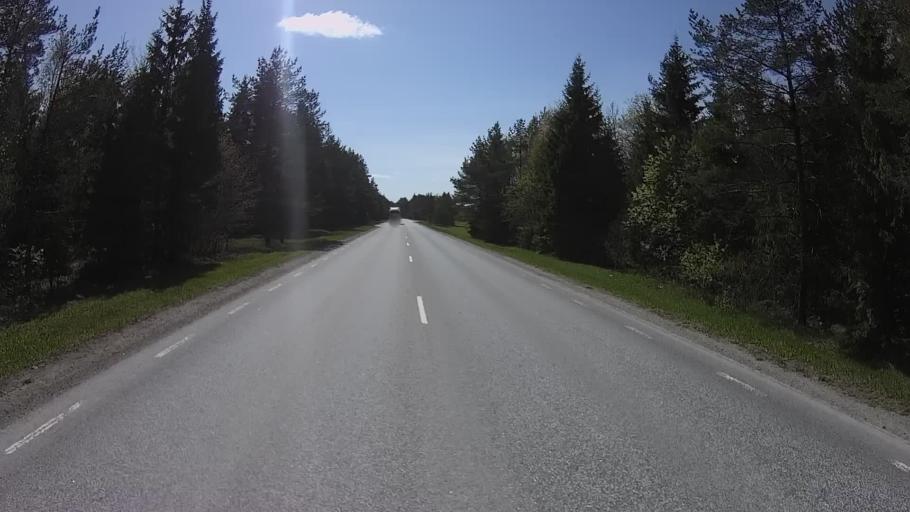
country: EE
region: Harju
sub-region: Keila linn
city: Keila
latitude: 59.2551
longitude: 24.2855
